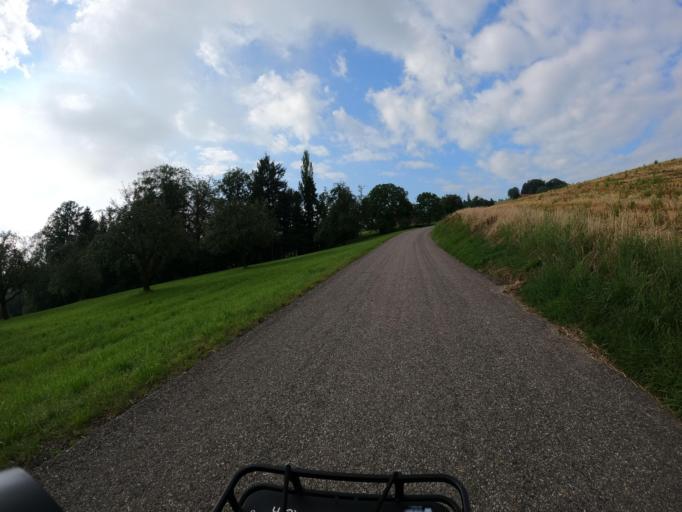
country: CH
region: Aargau
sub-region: Bezirk Muri
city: Buttwil
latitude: 47.2439
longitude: 8.3262
